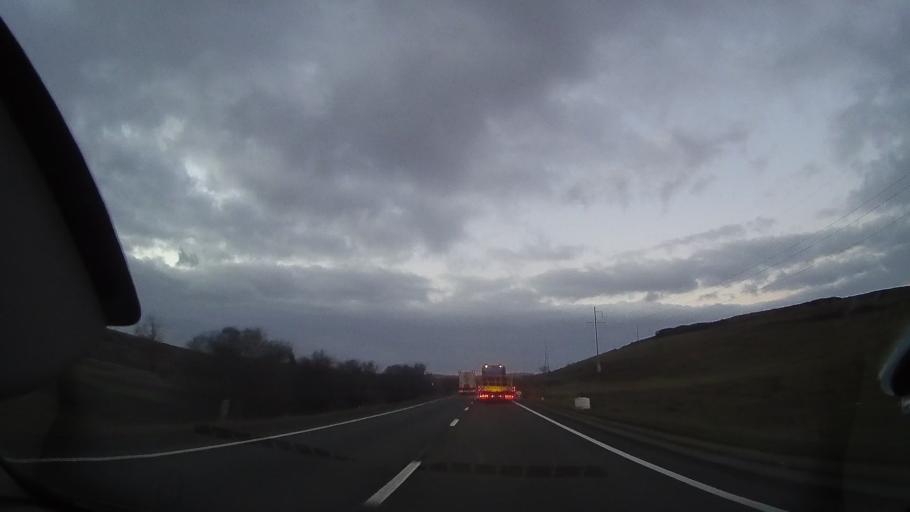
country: RO
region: Cluj
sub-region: Comuna Izvoru Crisului
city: Izvoru Crisului
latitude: 46.8478
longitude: 23.0827
